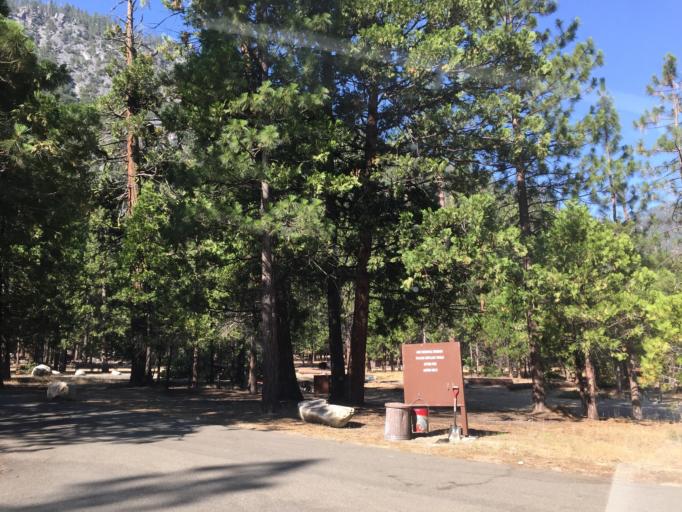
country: US
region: California
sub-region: Tulare County
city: Three Rivers
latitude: 36.7862
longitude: -118.6606
